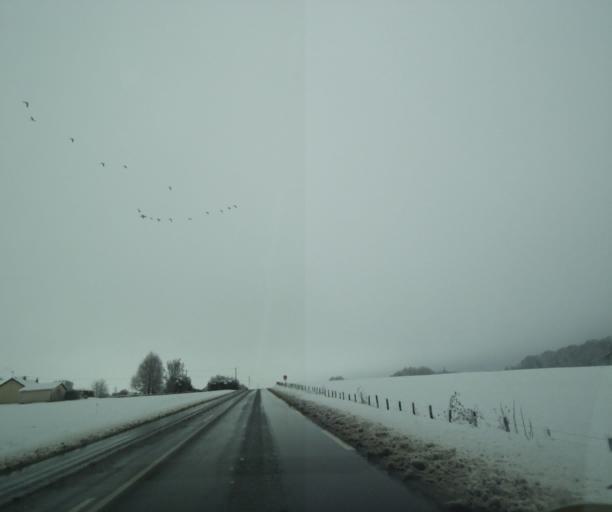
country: FR
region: Champagne-Ardenne
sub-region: Departement de la Haute-Marne
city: Montier-en-Der
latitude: 48.5387
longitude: 4.8221
